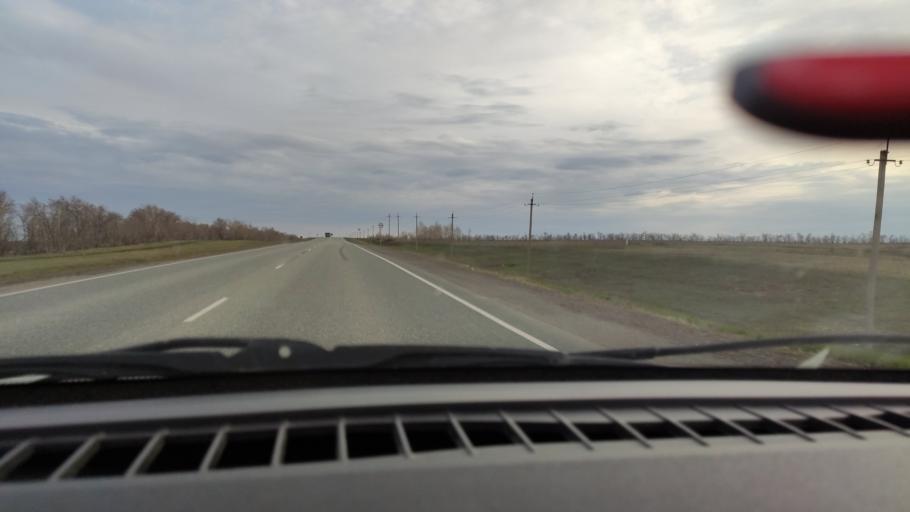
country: RU
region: Orenburg
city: Tatarskaya Kargala
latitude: 52.0059
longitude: 55.2010
